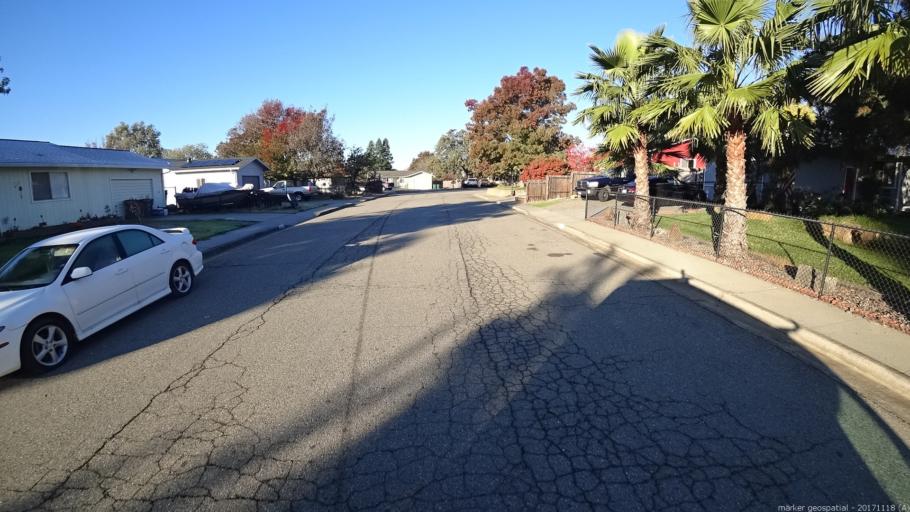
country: US
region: California
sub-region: Shasta County
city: Cottonwood
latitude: 40.3999
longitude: -122.2895
